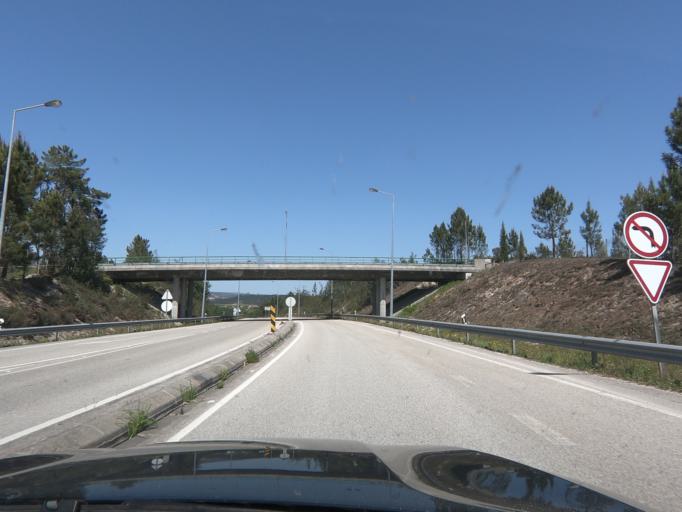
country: PT
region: Coimbra
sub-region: Lousa
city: Lousa
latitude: 40.1261
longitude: -8.2744
